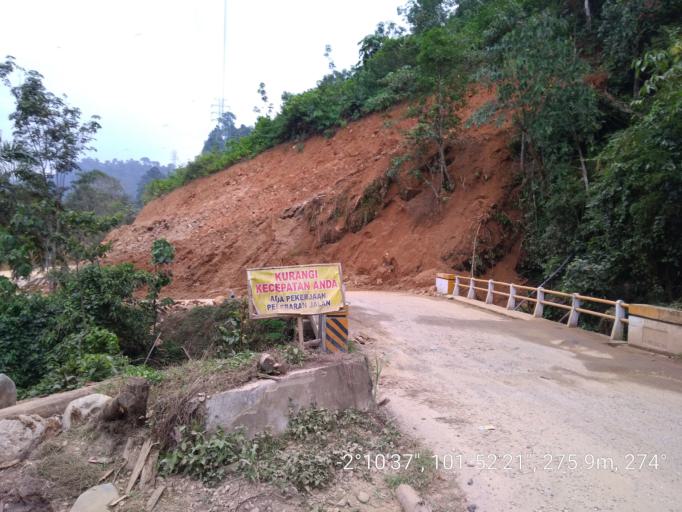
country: ID
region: Jambi
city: Muarasiau
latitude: -2.1770
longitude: 101.8727
